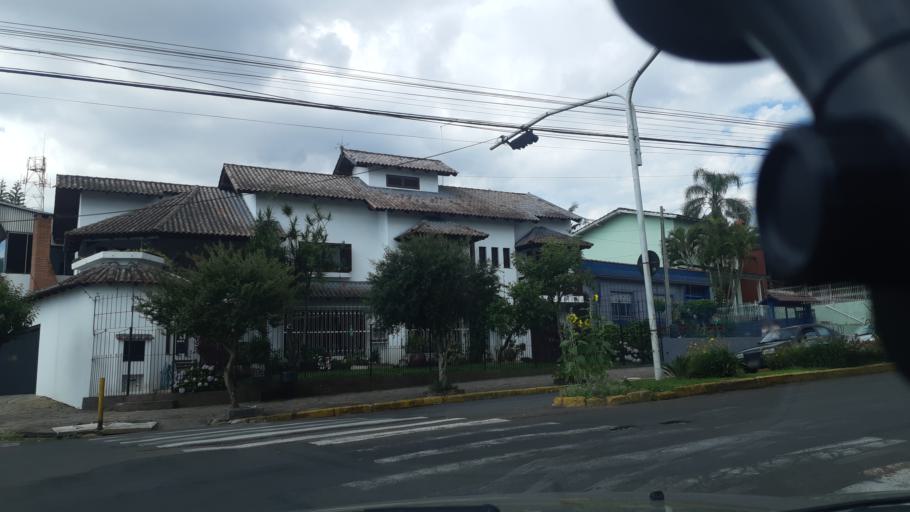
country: BR
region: Rio Grande do Sul
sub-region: Esteio
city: Esteio
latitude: -29.8492
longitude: -51.1677
